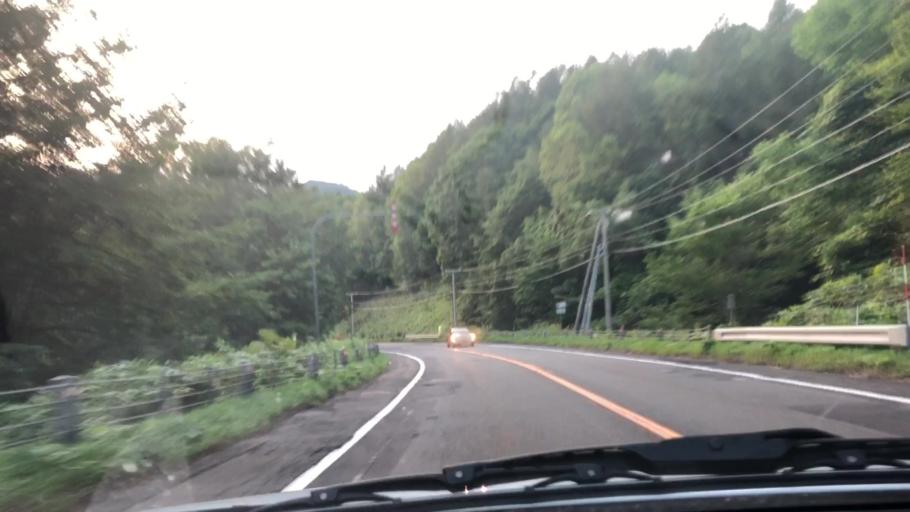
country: JP
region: Hokkaido
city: Shimo-furano
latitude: 42.8917
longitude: 142.1923
